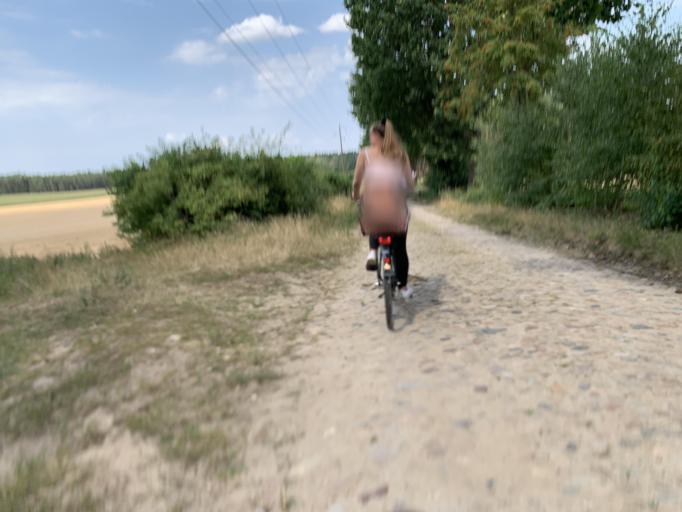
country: DE
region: Lower Saxony
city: Thomasburg
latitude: 53.2004
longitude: 10.6365
